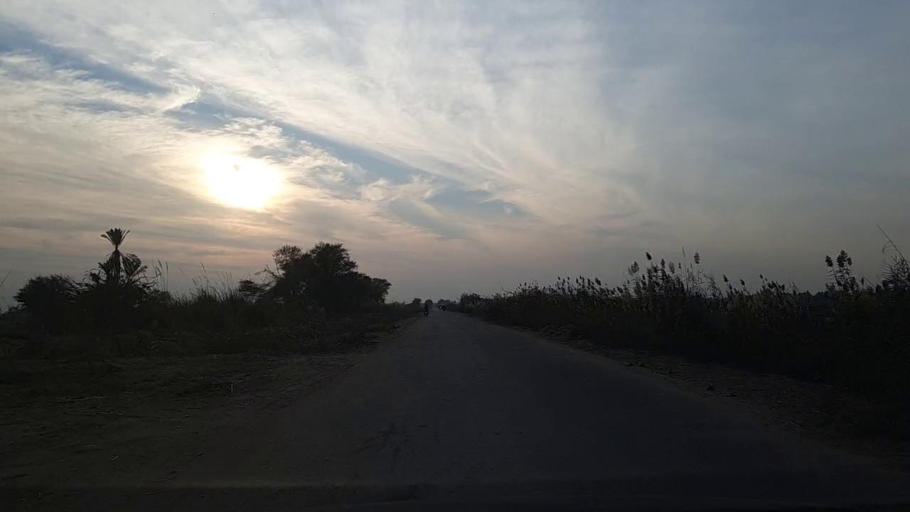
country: PK
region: Sindh
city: Daur
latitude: 26.3999
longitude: 68.4644
